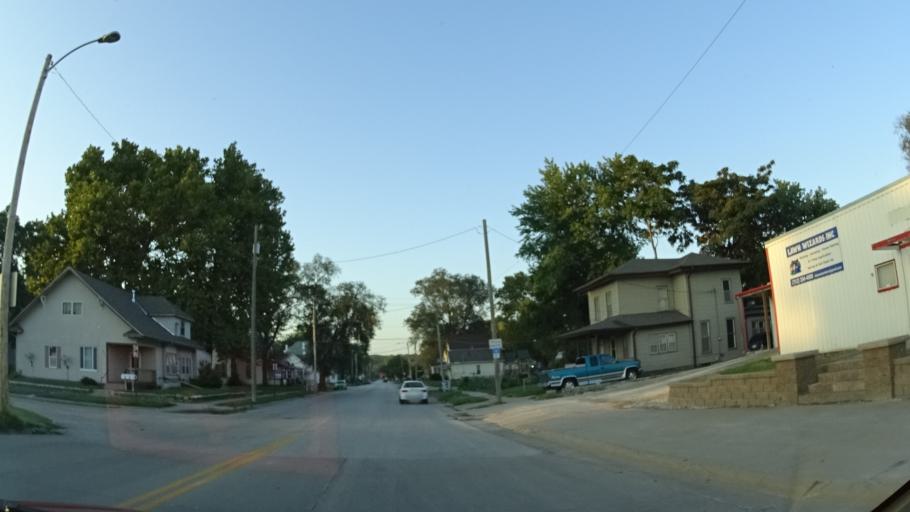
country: US
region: Iowa
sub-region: Pottawattamie County
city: Council Bluffs
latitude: 41.2625
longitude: -95.8560
